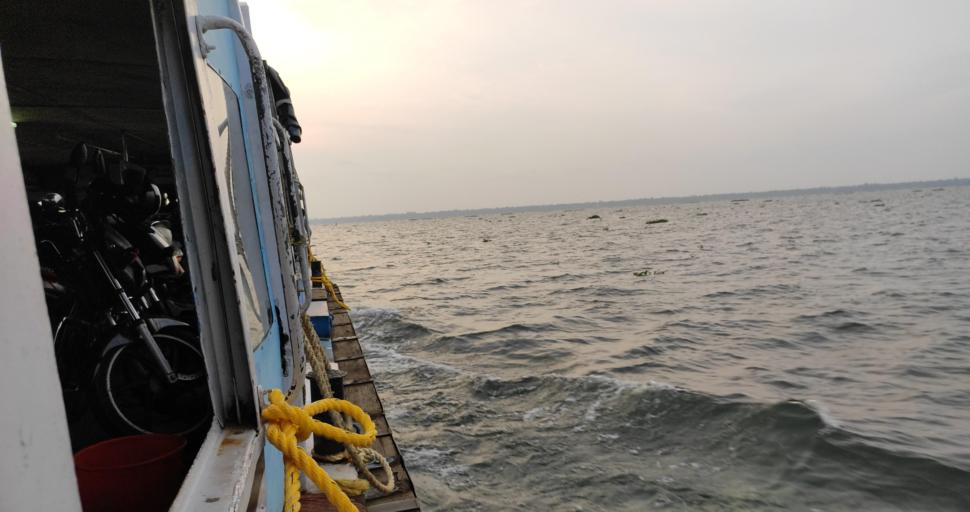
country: IN
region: Kerala
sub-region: Alappuzha
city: Shertallai
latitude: 9.6030
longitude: 76.3911
